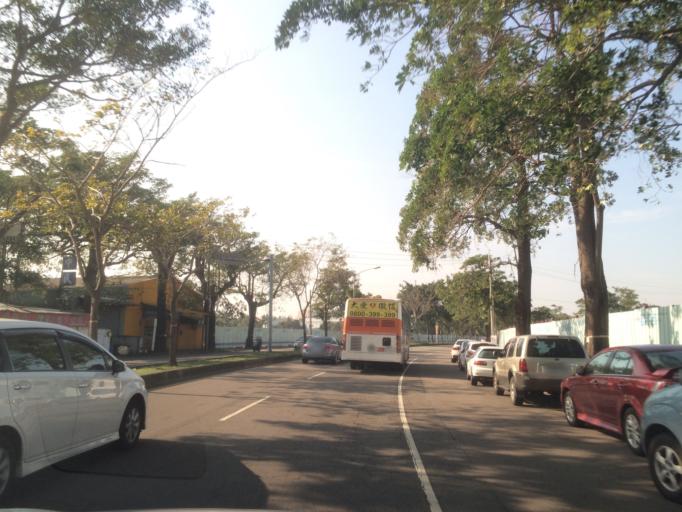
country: TW
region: Taiwan
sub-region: Taichung City
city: Taichung
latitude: 24.1821
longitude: 120.6809
